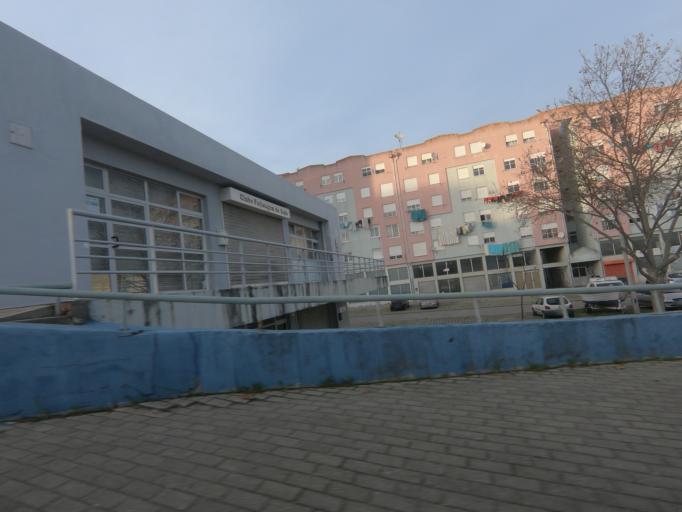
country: PT
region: Setubal
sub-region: Setubal
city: Setubal
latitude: 38.5302
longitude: -8.8655
